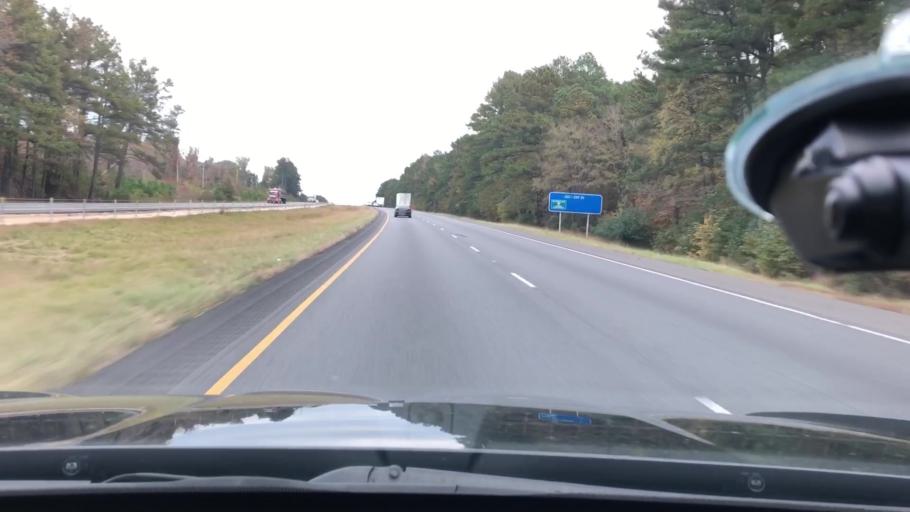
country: US
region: Arkansas
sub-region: Clark County
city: Arkadelphia
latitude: 34.2190
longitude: -93.0240
